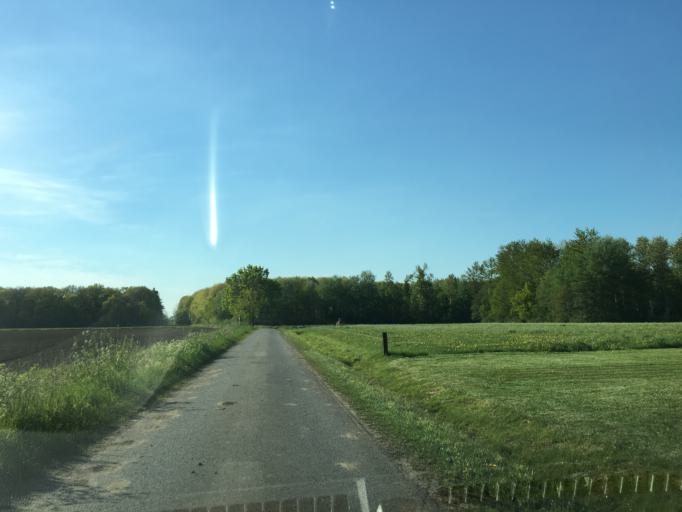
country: DE
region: North Rhine-Westphalia
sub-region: Regierungsbezirk Munster
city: Nordkirchen
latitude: 51.7591
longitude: 7.4968
